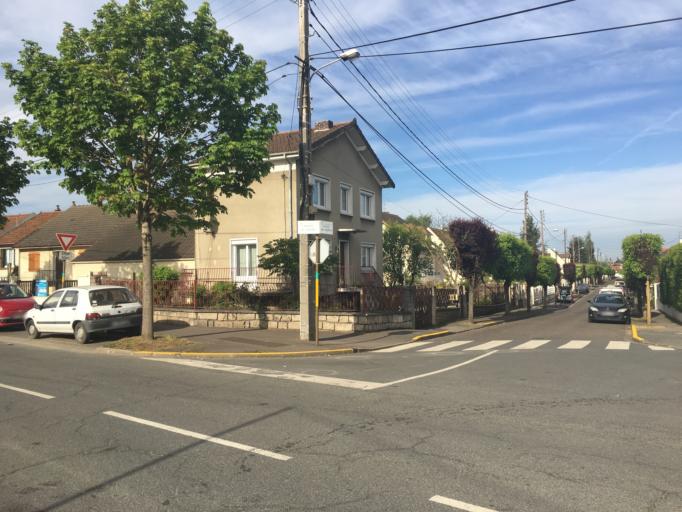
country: FR
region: Ile-de-France
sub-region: Departement de l'Essonne
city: Fleury-Merogis
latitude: 48.6531
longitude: 2.3693
